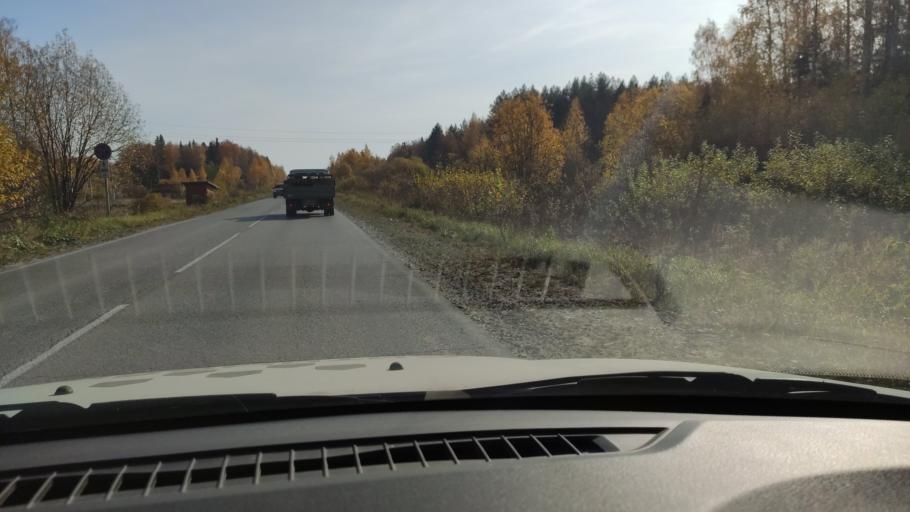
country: RU
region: Perm
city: Novyye Lyady
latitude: 58.0321
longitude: 56.6137
